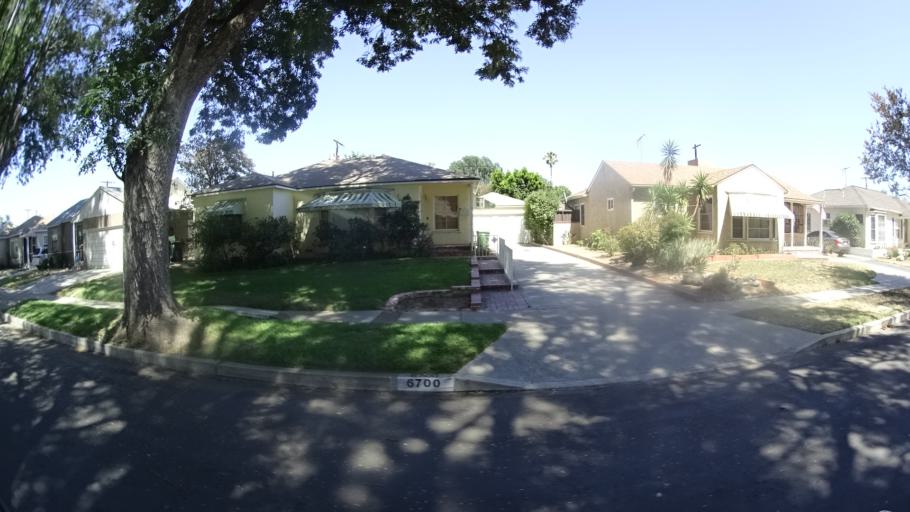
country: US
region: California
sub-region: Los Angeles County
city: Van Nuys
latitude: 34.1920
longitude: -118.4951
